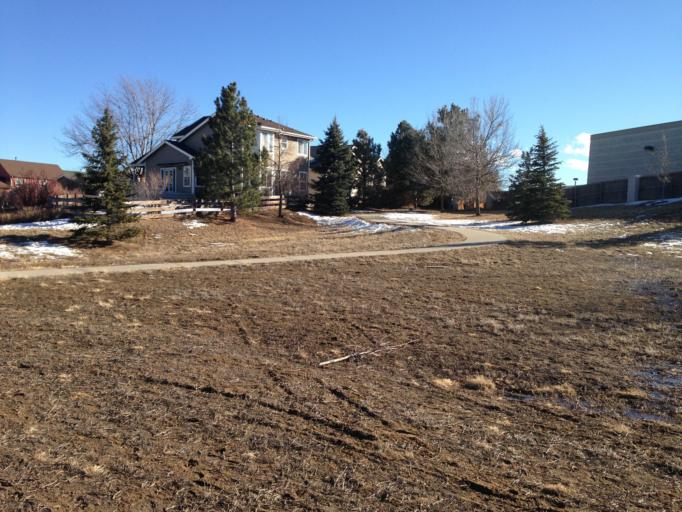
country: US
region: Colorado
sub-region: Boulder County
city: Lafayette
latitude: 40.0175
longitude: -105.1003
